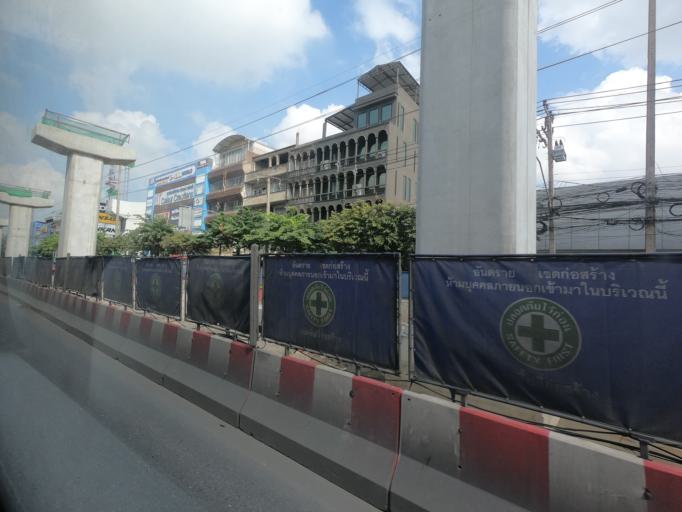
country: TH
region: Bangkok
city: Wang Thonglang
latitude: 13.7885
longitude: 100.6050
